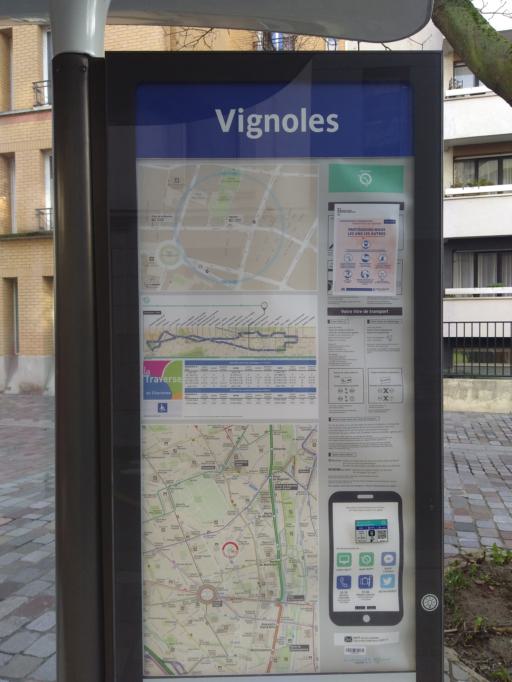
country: FR
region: Ile-de-France
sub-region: Departement de Seine-Saint-Denis
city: Bagnolet
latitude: 48.8543
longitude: 2.4003
